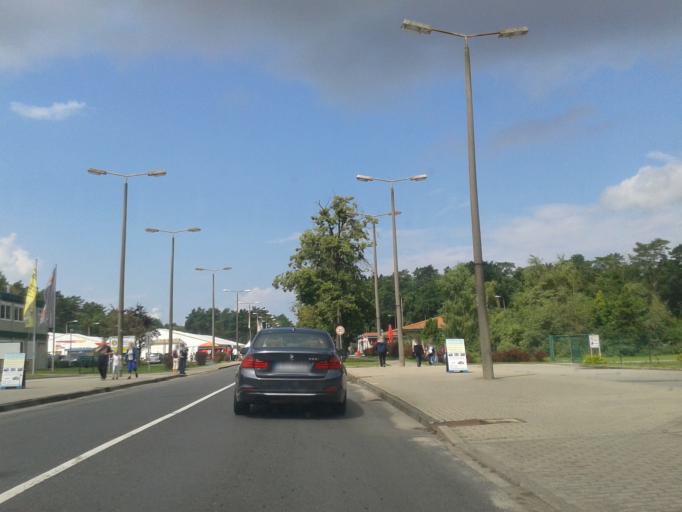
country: PL
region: West Pomeranian Voivodeship
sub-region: Swinoujscie
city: Swinoujscie
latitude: 53.9222
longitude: 14.2172
